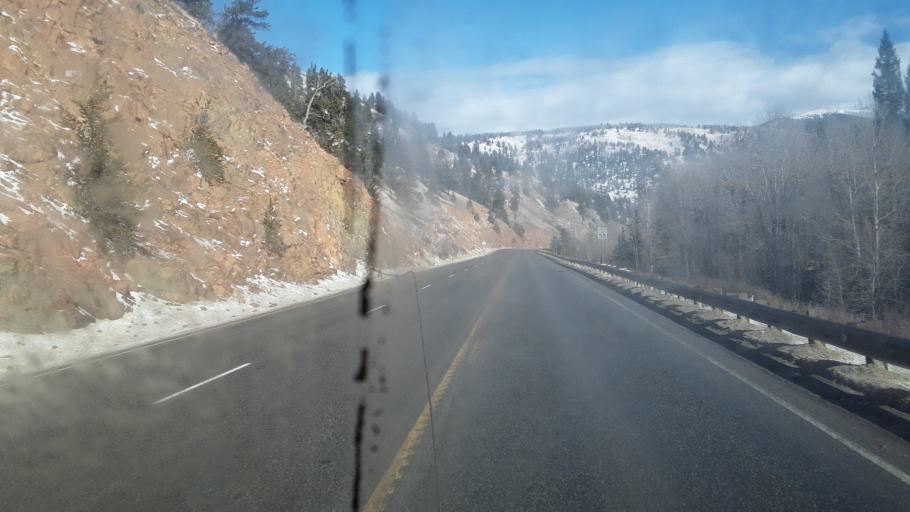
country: US
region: Colorado
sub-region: Clear Creek County
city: Georgetown
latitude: 39.4490
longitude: -105.7319
